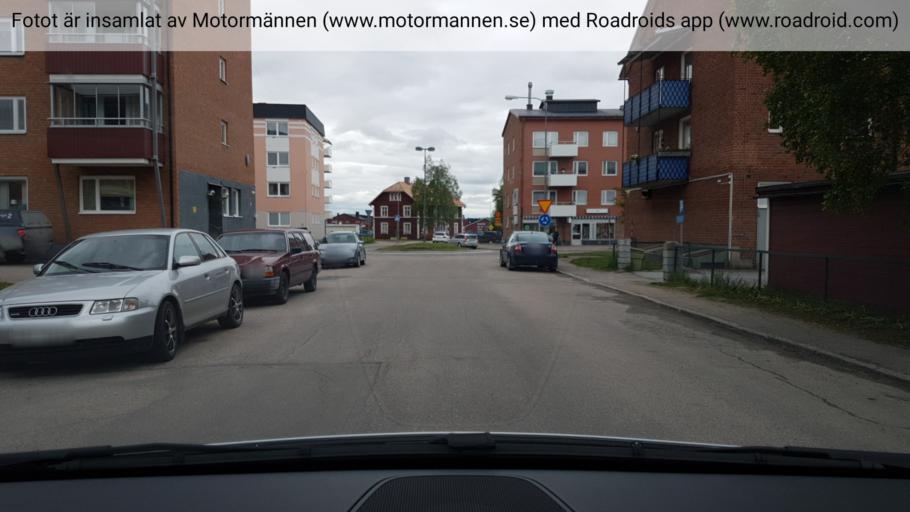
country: SE
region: Norrbotten
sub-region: Gallivare Kommun
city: Gaellivare
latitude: 67.1346
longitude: 20.6549
